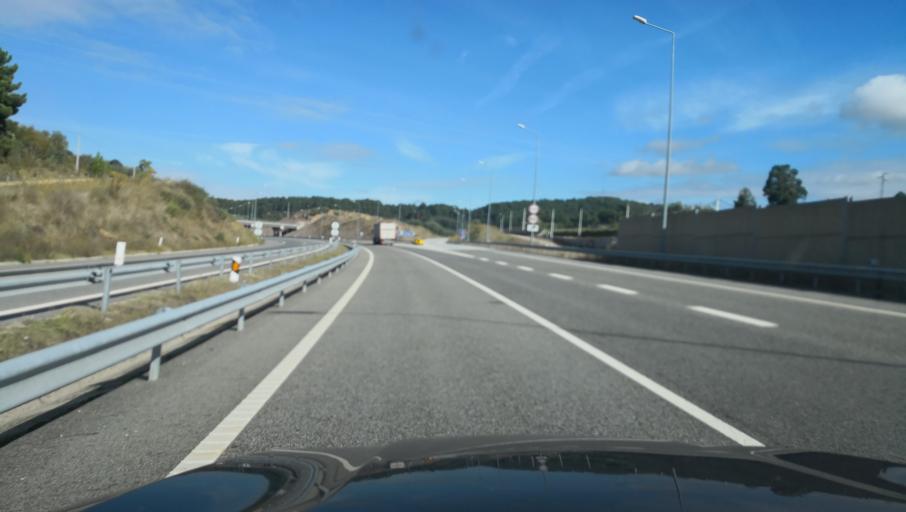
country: PT
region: Vila Real
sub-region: Boticas
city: Boticas
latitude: 41.6457
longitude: -7.5848
